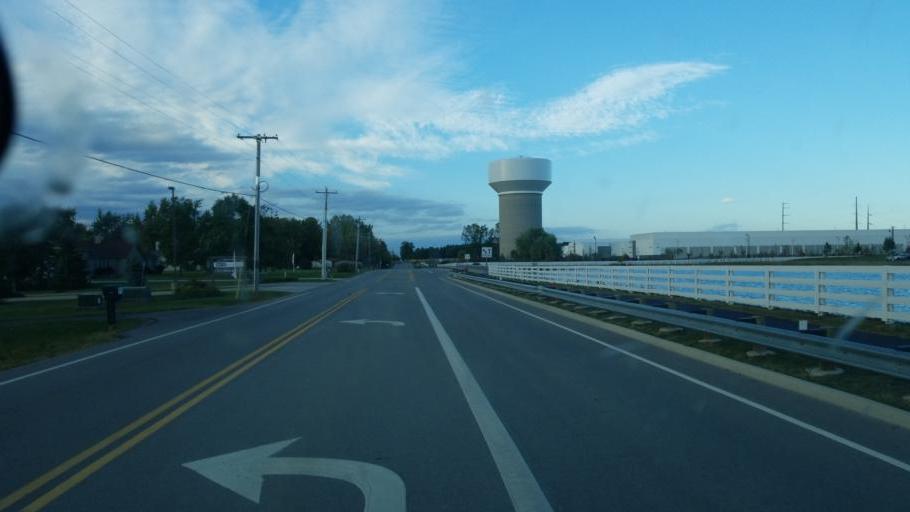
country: US
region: Ohio
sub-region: Franklin County
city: New Albany
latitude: 40.0907
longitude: -82.7543
